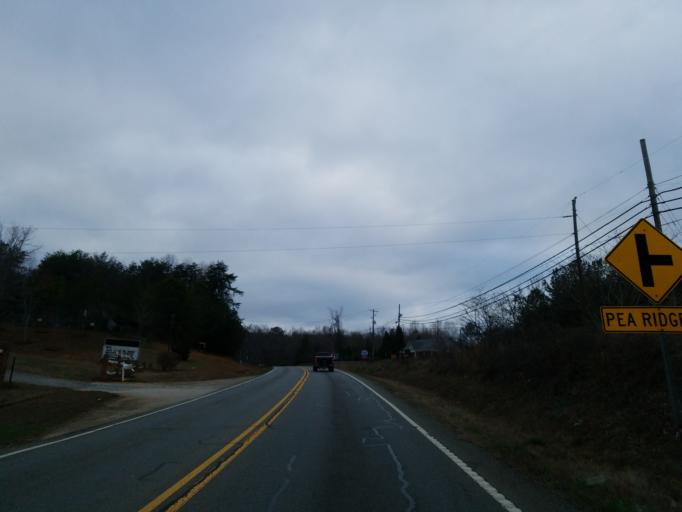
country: US
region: Georgia
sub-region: Cherokee County
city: Canton
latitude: 34.2698
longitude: -84.4966
